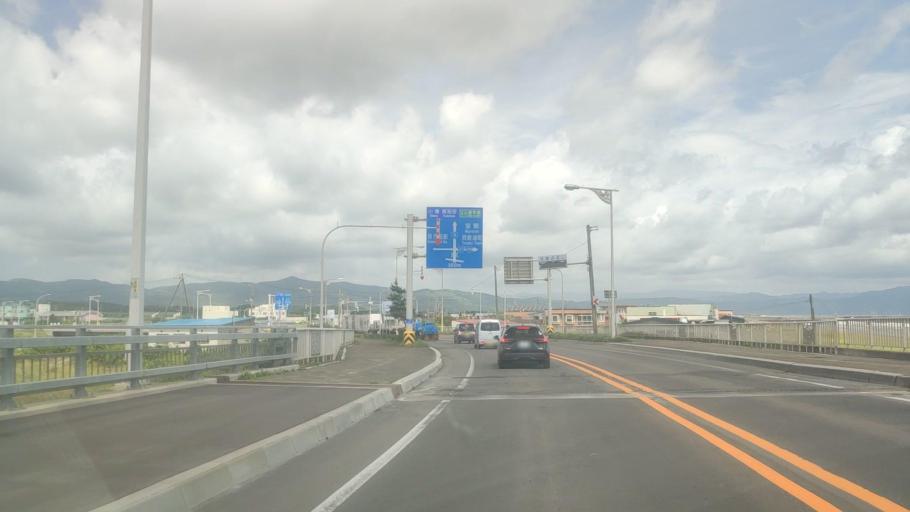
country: JP
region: Hokkaido
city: Niseko Town
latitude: 42.5153
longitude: 140.3823
